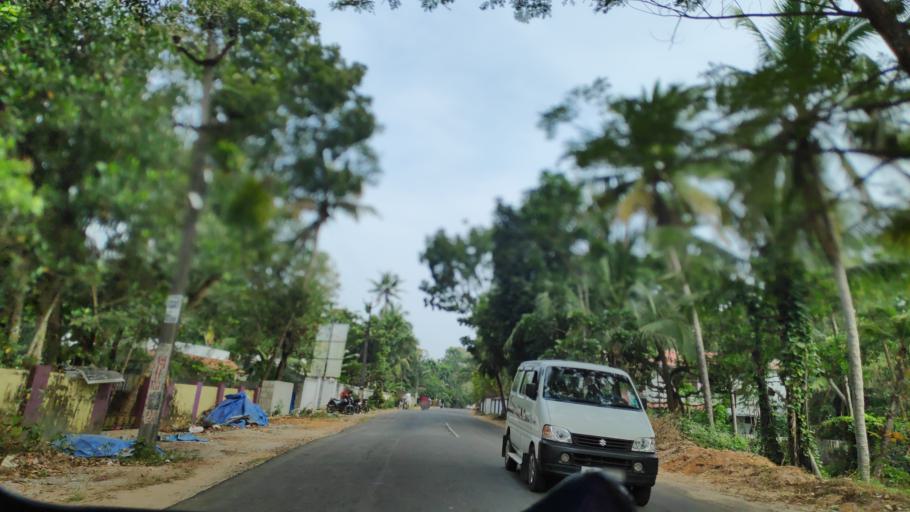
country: IN
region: Kerala
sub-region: Kottayam
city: Vaikam
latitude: 9.7409
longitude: 76.3628
